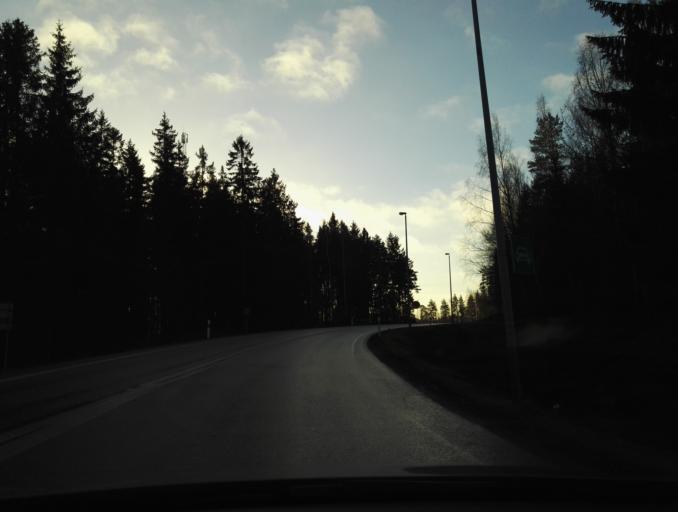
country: SE
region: Kronoberg
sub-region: Vaxjo Kommun
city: Vaexjoe
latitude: 56.9032
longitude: 14.7952
